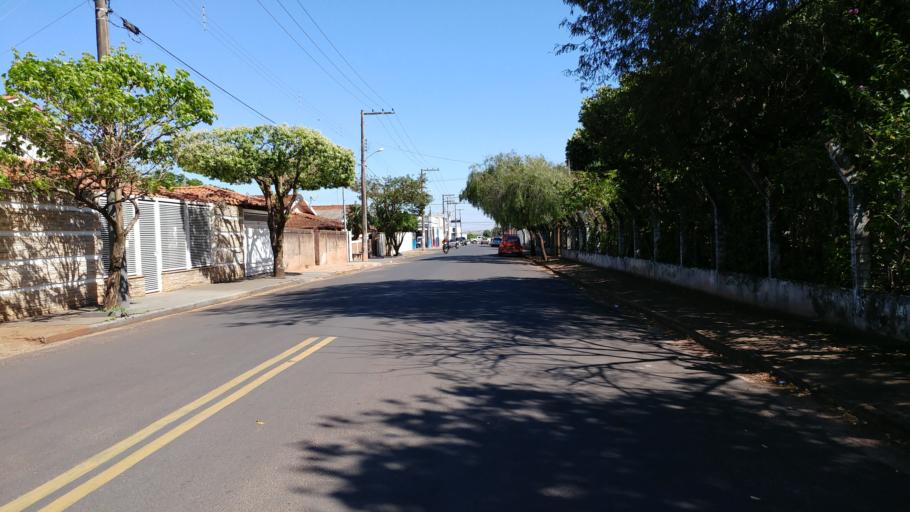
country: BR
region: Sao Paulo
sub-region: Paraguacu Paulista
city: Paraguacu Paulista
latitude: -22.4269
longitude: -50.5819
